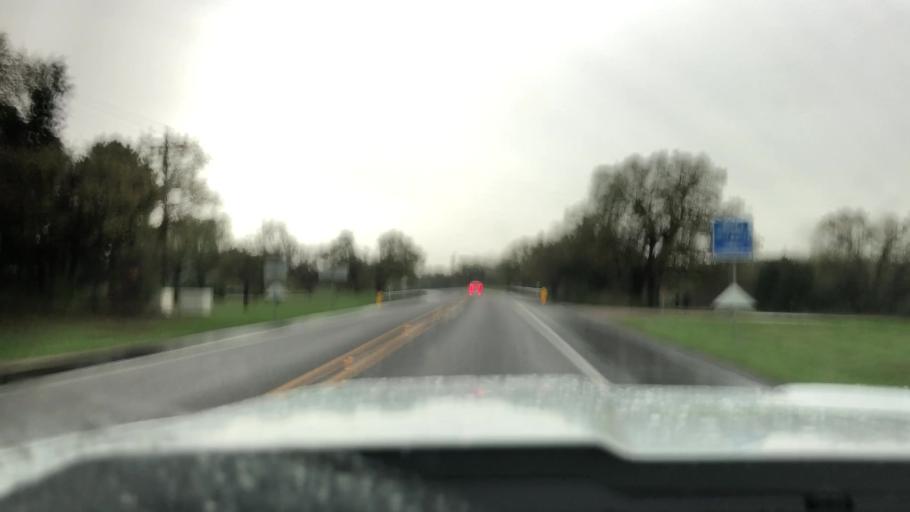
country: US
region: Texas
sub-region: Johnson County
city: Keene
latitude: 32.4189
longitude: -97.3198
